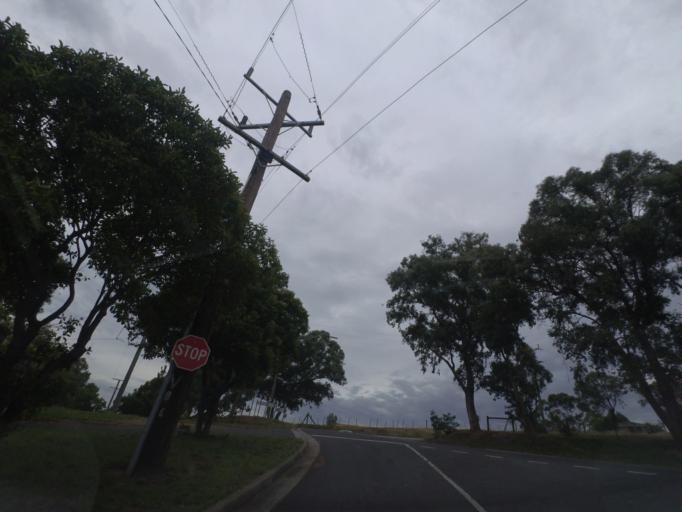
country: AU
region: Victoria
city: Plenty
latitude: -37.6595
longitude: 145.1290
